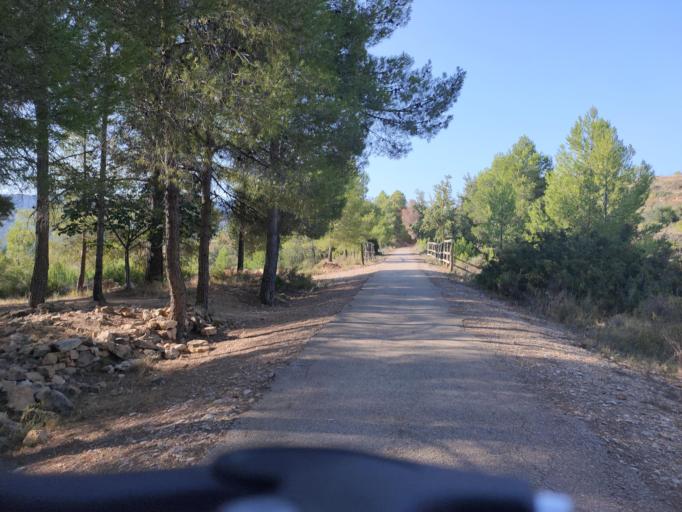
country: ES
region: Catalonia
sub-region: Provincia de Tarragona
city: Bot
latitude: 41.0047
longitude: 0.3751
